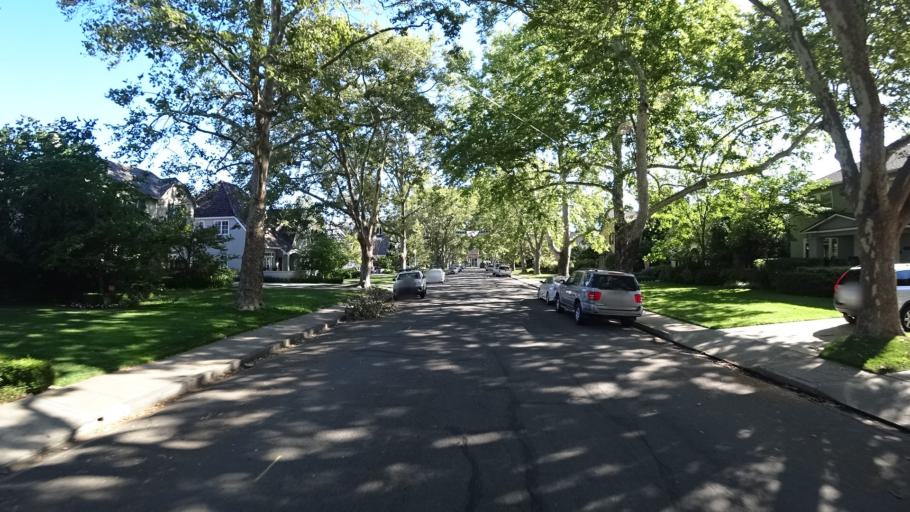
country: US
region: California
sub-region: Sacramento County
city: Sacramento
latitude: 38.5675
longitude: -121.4524
